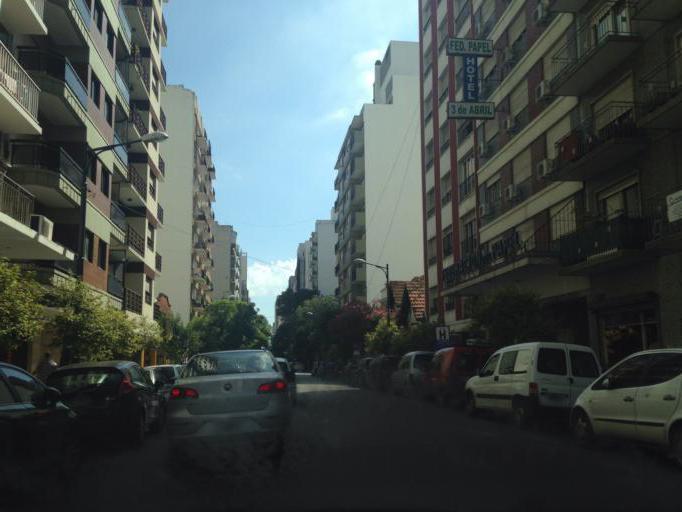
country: AR
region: Buenos Aires
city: Mar del Plata
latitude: -38.0034
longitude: -57.5501
